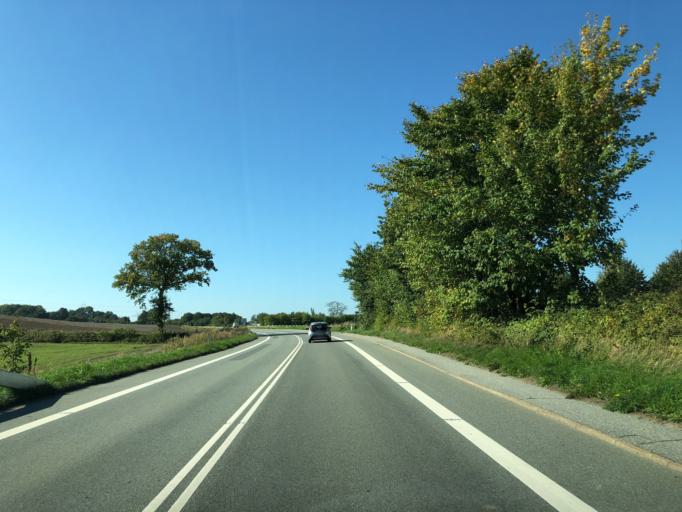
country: DK
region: South Denmark
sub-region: Aabenraa Kommune
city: Aabenraa
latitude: 55.0163
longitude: 9.4446
